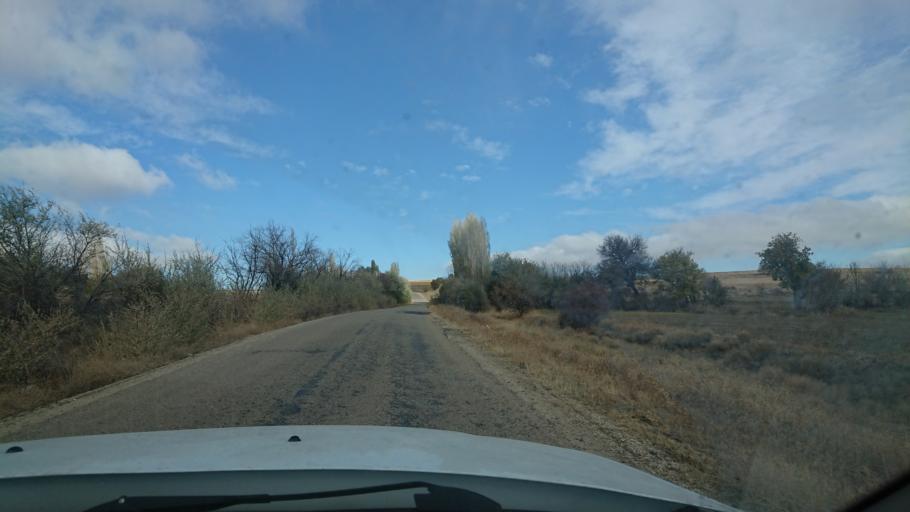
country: TR
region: Aksaray
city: Agacoren
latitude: 38.8310
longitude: 33.9559
